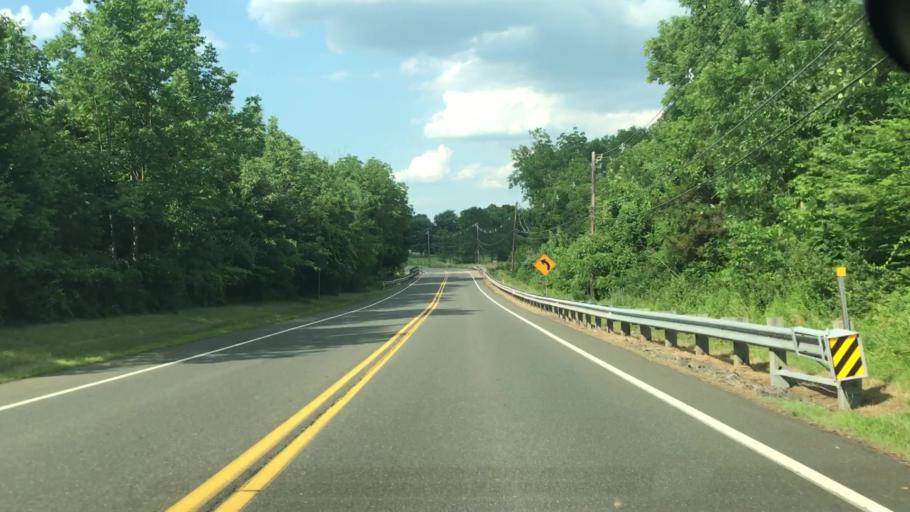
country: US
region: New Jersey
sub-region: Hunterdon County
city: Flemington
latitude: 40.4664
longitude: -74.8280
